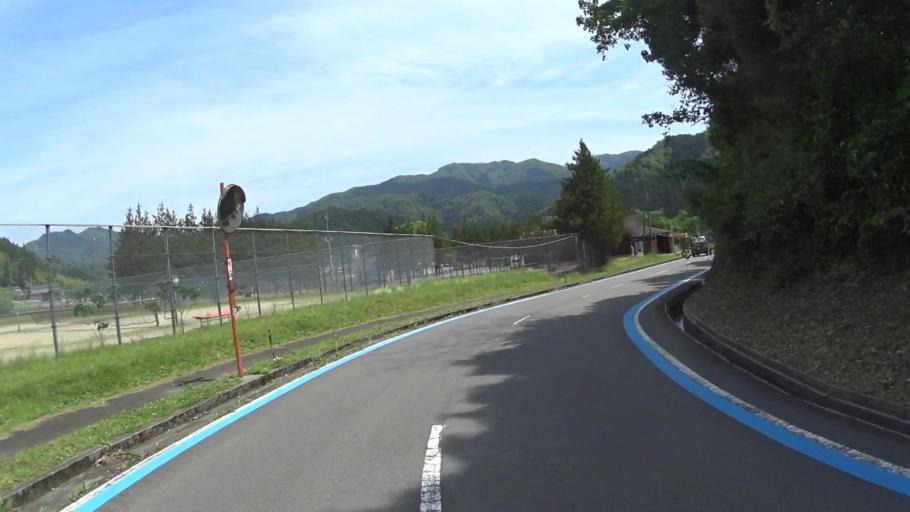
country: JP
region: Kyoto
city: Maizuru
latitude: 35.3734
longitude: 135.4373
